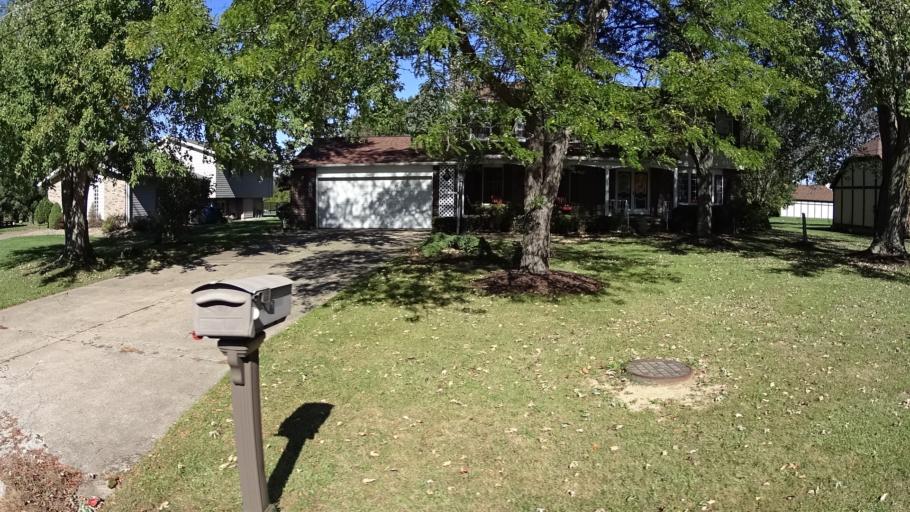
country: US
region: Ohio
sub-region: Lorain County
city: Amherst
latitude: 41.4112
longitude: -82.2216
